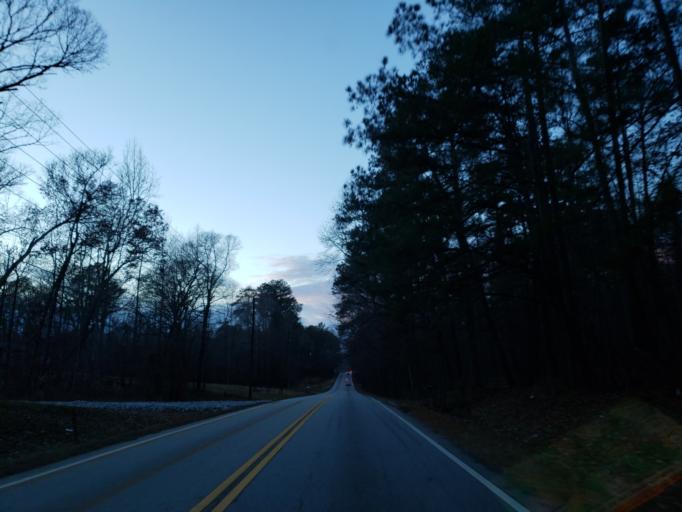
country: US
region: Georgia
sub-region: Douglas County
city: Lithia Springs
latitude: 33.6898
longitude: -84.6071
